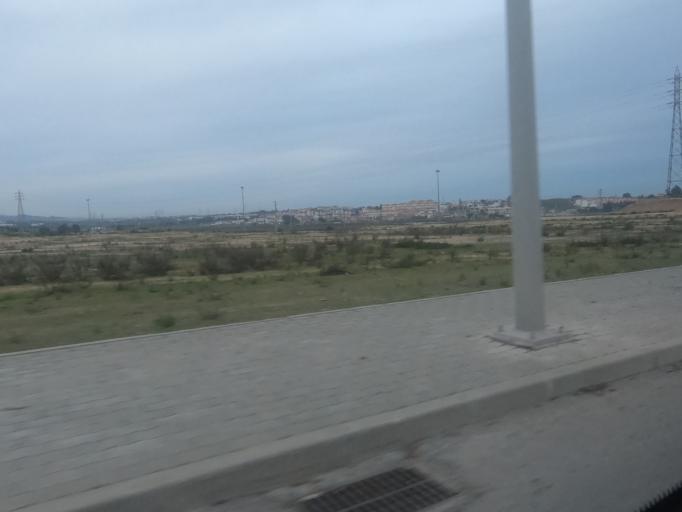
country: PT
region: Setubal
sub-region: Setubal
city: Setubal
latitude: 38.5083
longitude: -8.8341
